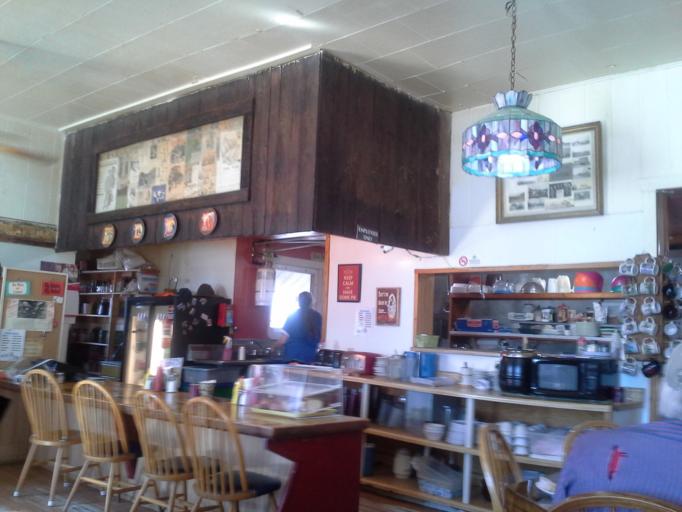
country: US
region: Montana
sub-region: Beaverhead County
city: Dillon
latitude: 44.7257
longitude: -112.6996
